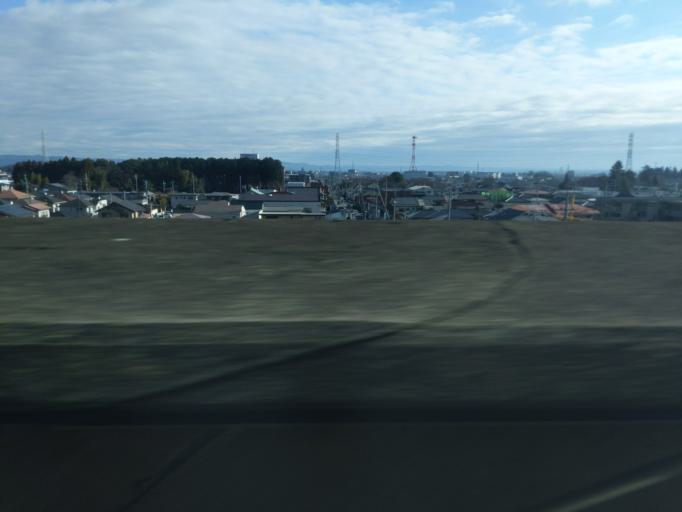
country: JP
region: Tochigi
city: Otawara
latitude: 36.8858
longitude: 139.9876
